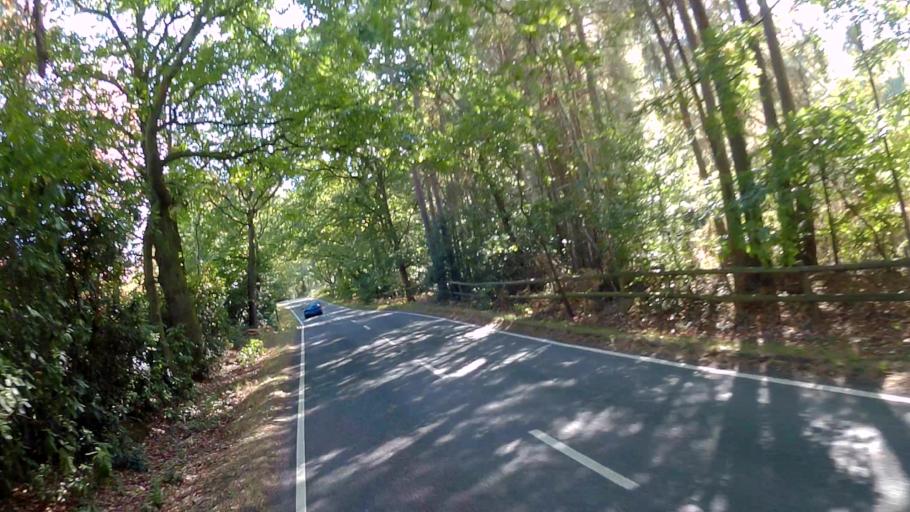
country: GB
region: England
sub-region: Surrey
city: Farnham
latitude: 51.1937
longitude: -0.7712
